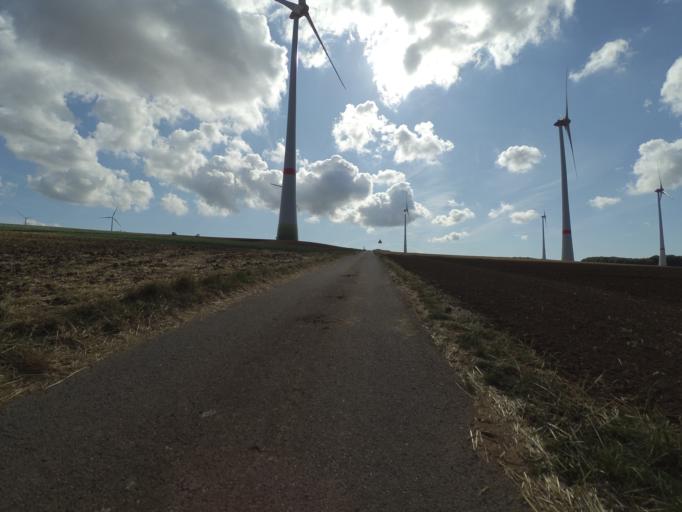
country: DE
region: Rheinland-Pfalz
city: Kirf
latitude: 49.5209
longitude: 6.4342
